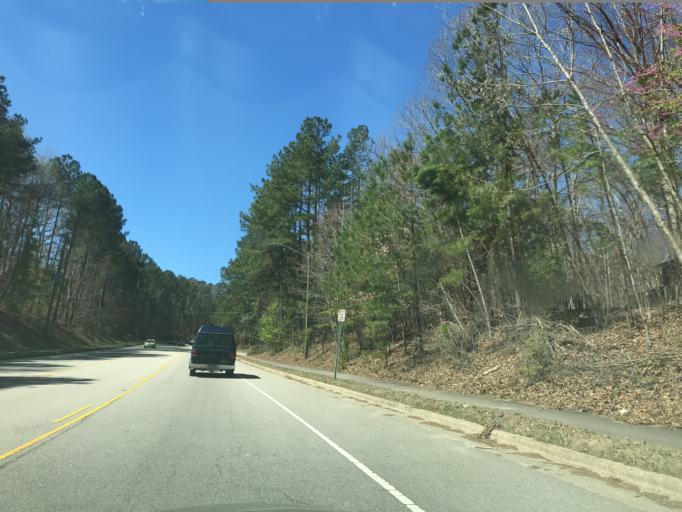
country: US
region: North Carolina
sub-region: Wake County
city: West Raleigh
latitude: 35.7669
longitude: -78.7020
